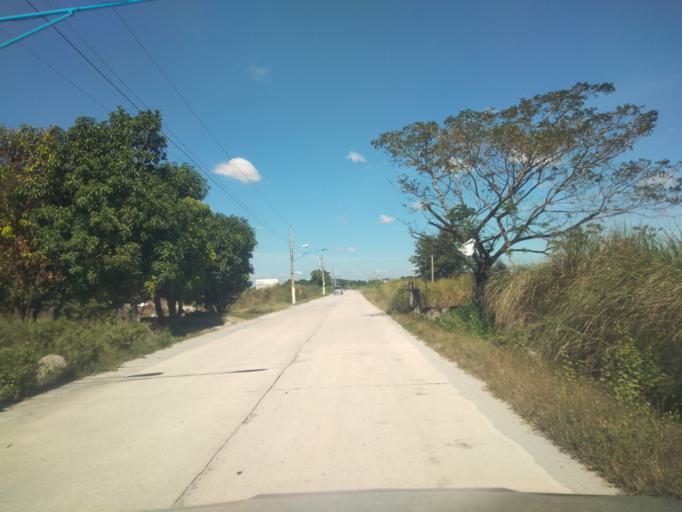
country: PH
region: Central Luzon
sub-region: Province of Pampanga
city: Balas
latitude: 15.0445
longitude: 120.6138
